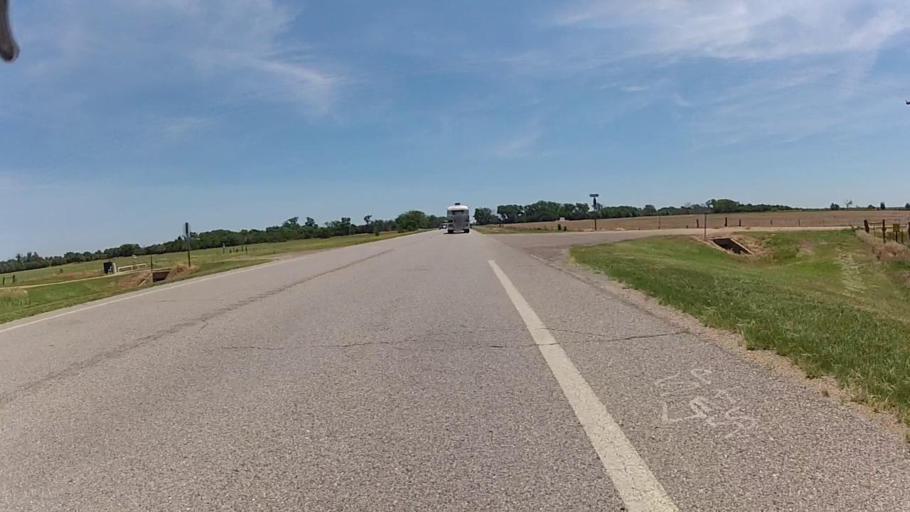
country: US
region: Kansas
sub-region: Barber County
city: Medicine Lodge
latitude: 37.2534
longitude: -98.4600
